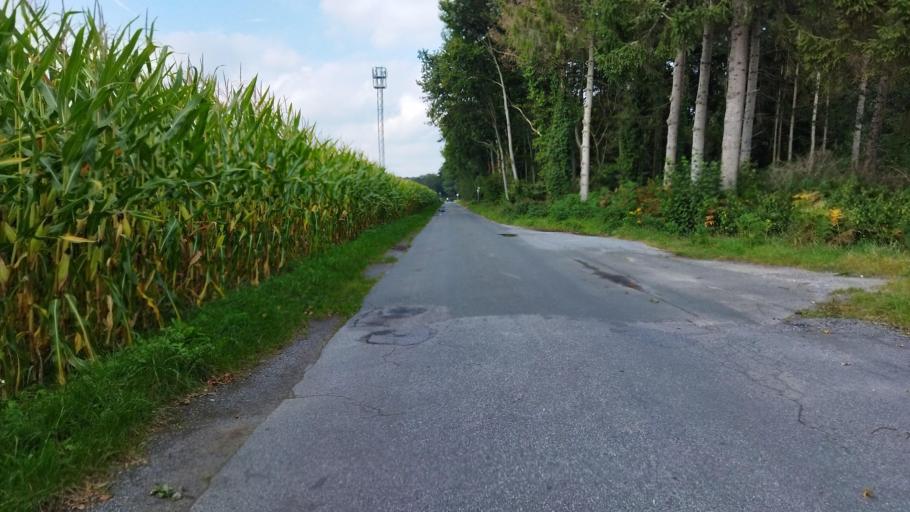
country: DE
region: North Rhine-Westphalia
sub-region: Regierungsbezirk Munster
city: Warendorf
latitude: 51.9596
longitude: 7.9404
